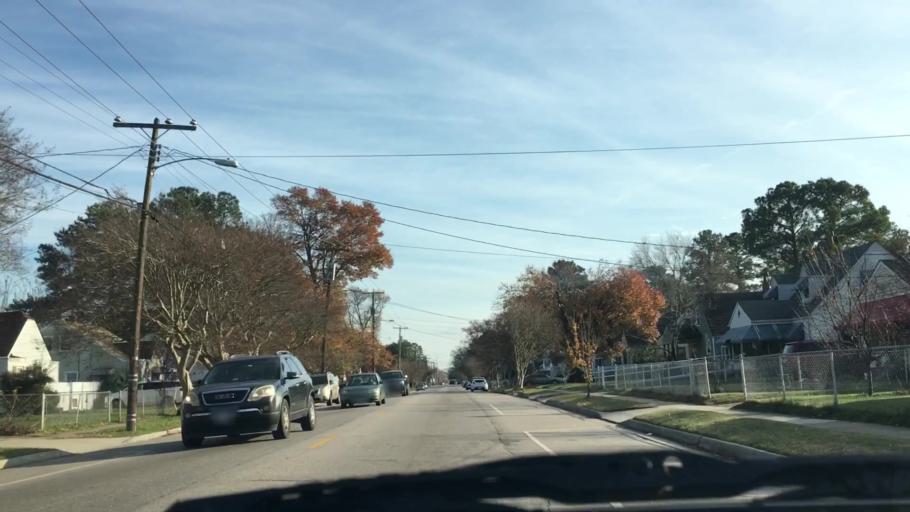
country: US
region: Virginia
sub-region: City of Norfolk
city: Norfolk
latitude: 36.8849
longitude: -76.2586
